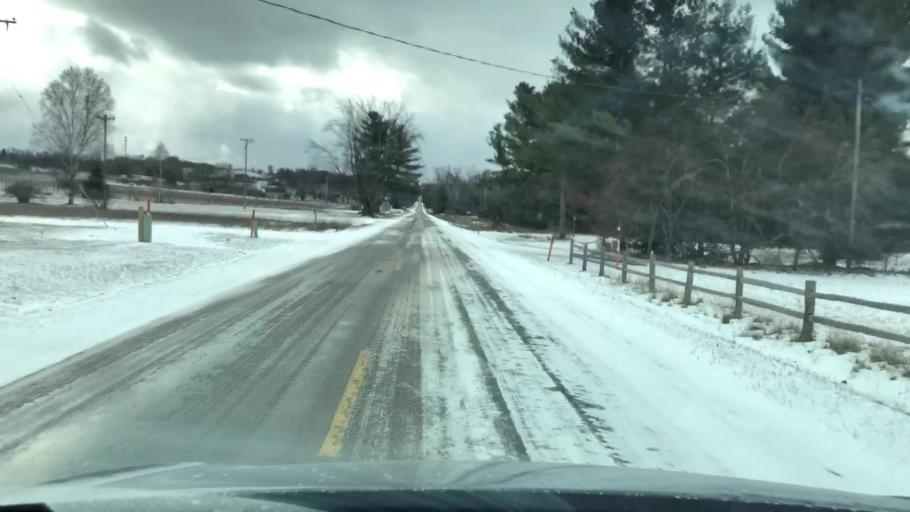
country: US
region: Michigan
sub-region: Antrim County
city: Elk Rapids
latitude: 44.9099
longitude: -85.5154
